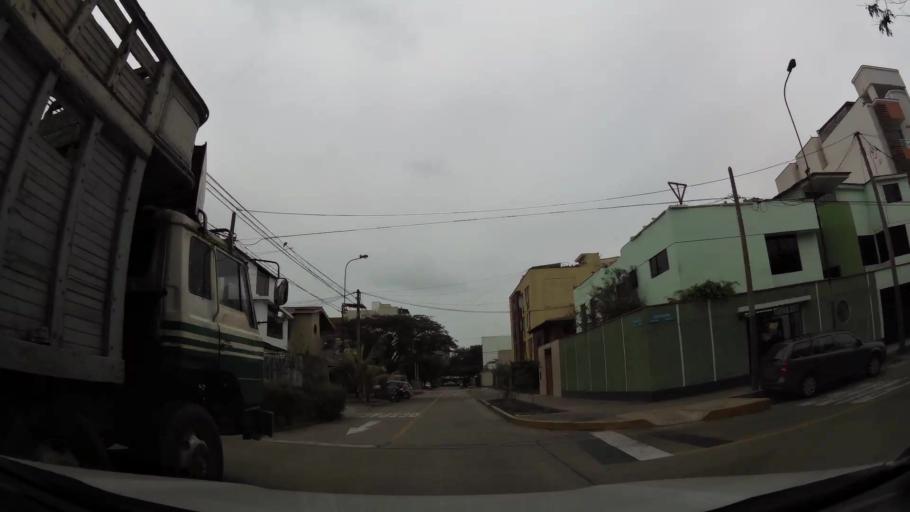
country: PE
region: Lima
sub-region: Lima
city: San Luis
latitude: -12.0994
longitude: -77.0075
